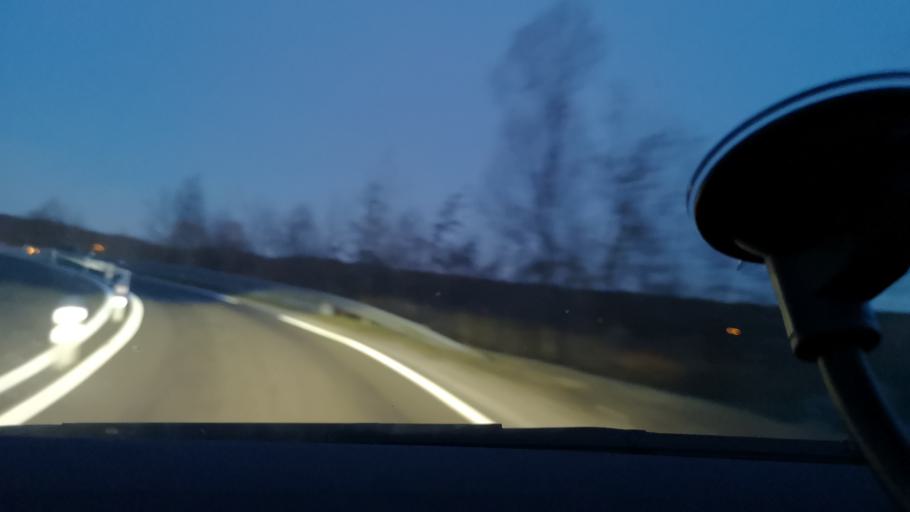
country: FR
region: Franche-Comte
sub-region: Departement du Jura
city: Champagnole
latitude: 46.7450
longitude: 5.9248
